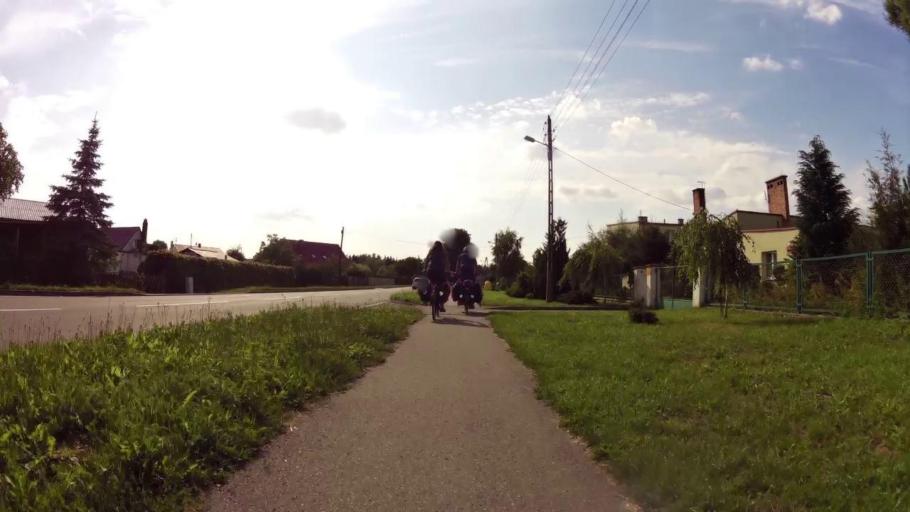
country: PL
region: West Pomeranian Voivodeship
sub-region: Powiat lobeski
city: Wegorzyno
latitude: 53.5525
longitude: 15.5322
